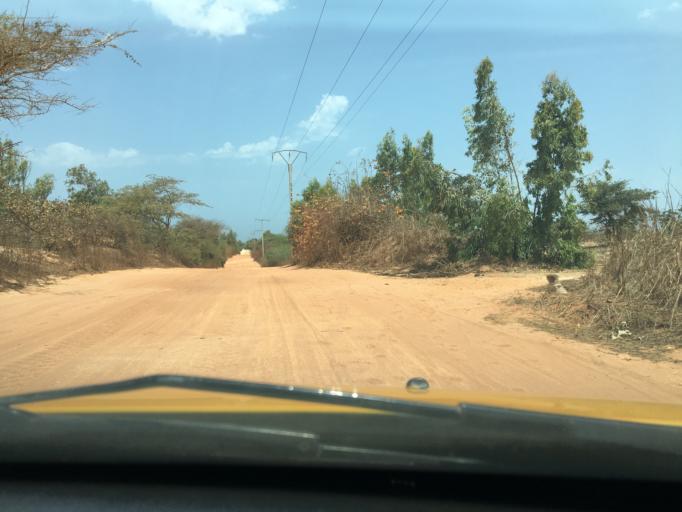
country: SN
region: Thies
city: Thies
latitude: 14.8183
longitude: -17.1988
